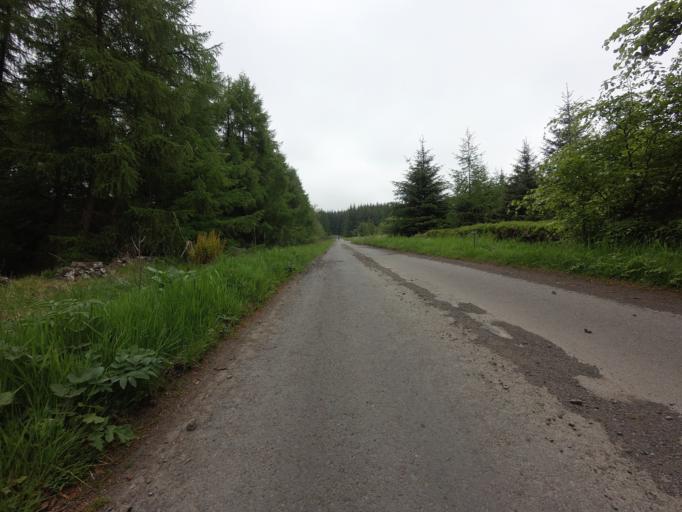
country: GB
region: Scotland
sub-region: Fife
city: Townhill
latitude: 56.1389
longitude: -3.4448
